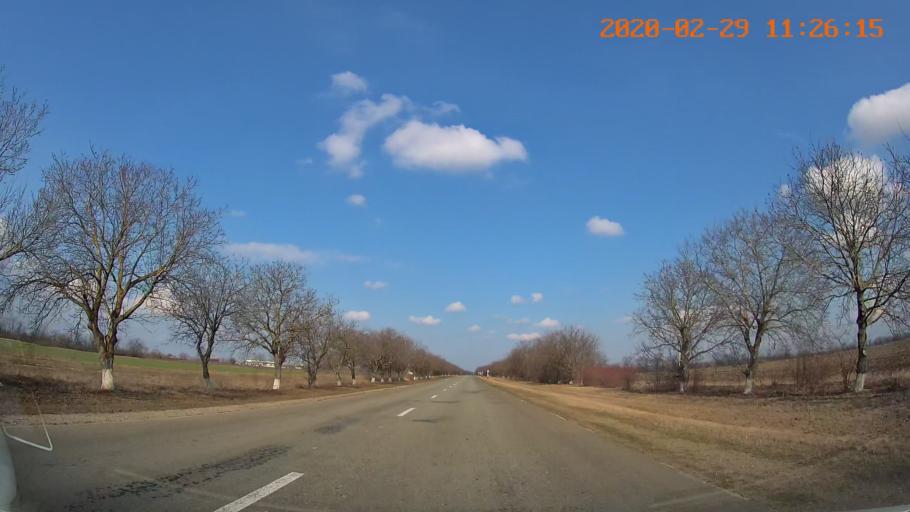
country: MD
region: Telenesti
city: Cocieri
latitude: 47.4506
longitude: 29.1468
